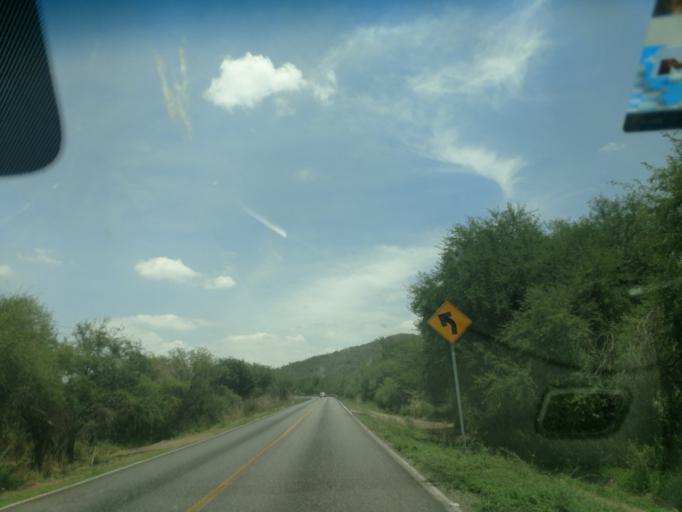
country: MX
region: San Luis Potosi
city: Ciudad Fernandez
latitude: 21.9956
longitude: -100.1377
